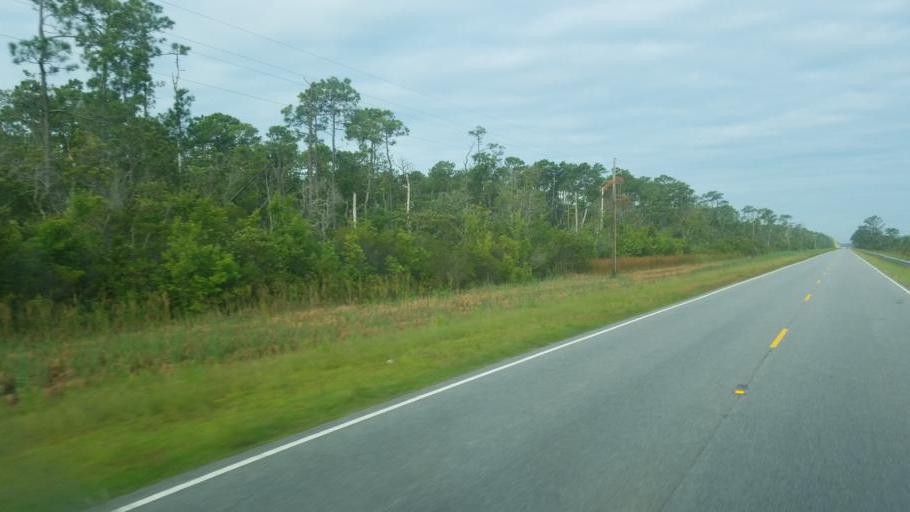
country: US
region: North Carolina
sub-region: Dare County
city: Manteo
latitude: 35.8694
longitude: -75.8035
